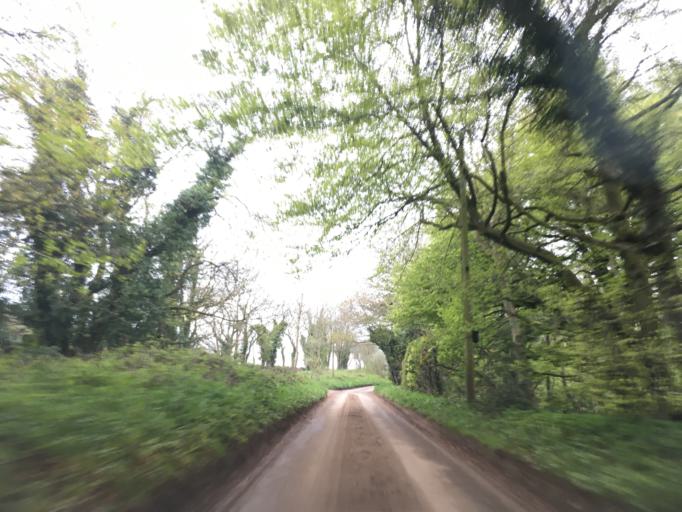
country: GB
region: England
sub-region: Gloucestershire
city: Wotton-under-Edge
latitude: 51.6394
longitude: -2.3207
